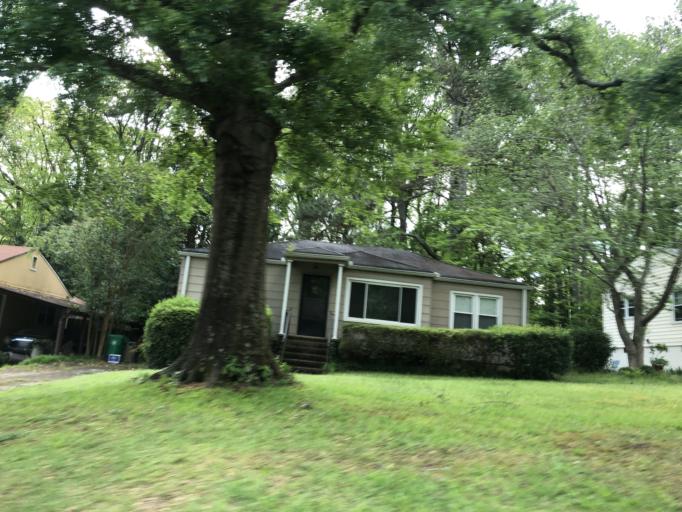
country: US
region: Georgia
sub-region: DeKalb County
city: North Druid Hills
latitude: 33.8121
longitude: -84.3405
